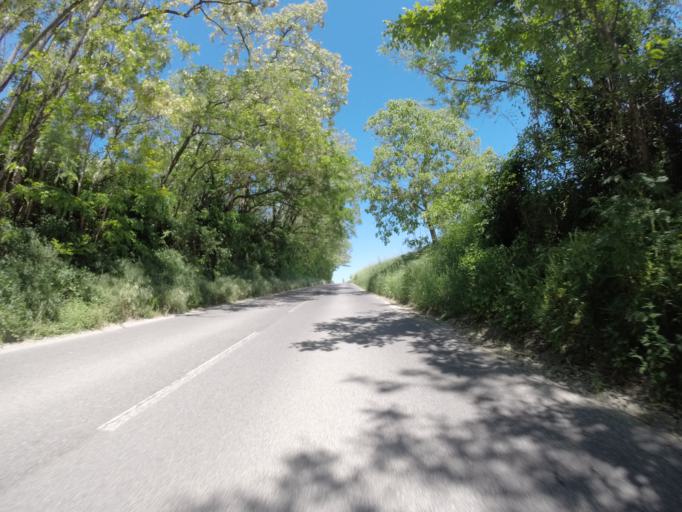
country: SK
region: Trnavsky
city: Hlohovec
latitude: 48.4680
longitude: 17.8546
